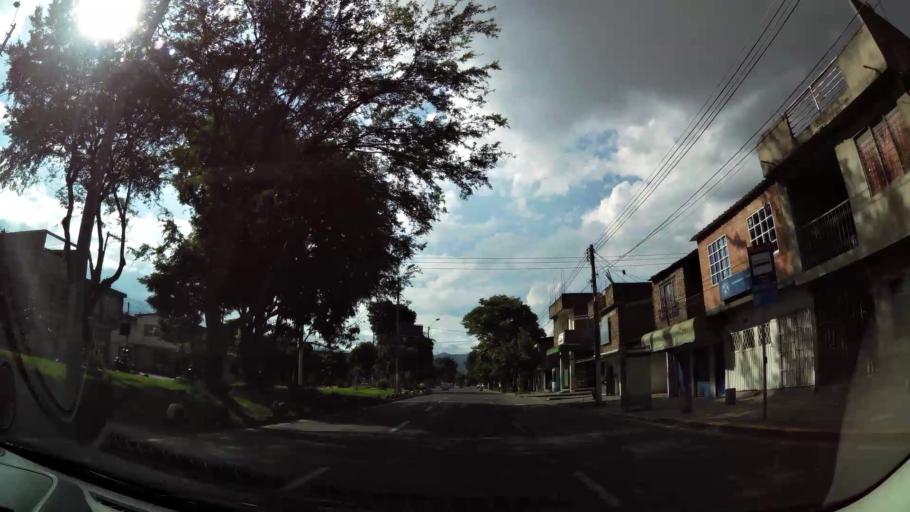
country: CO
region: Valle del Cauca
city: Cali
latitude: 3.4101
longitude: -76.4991
